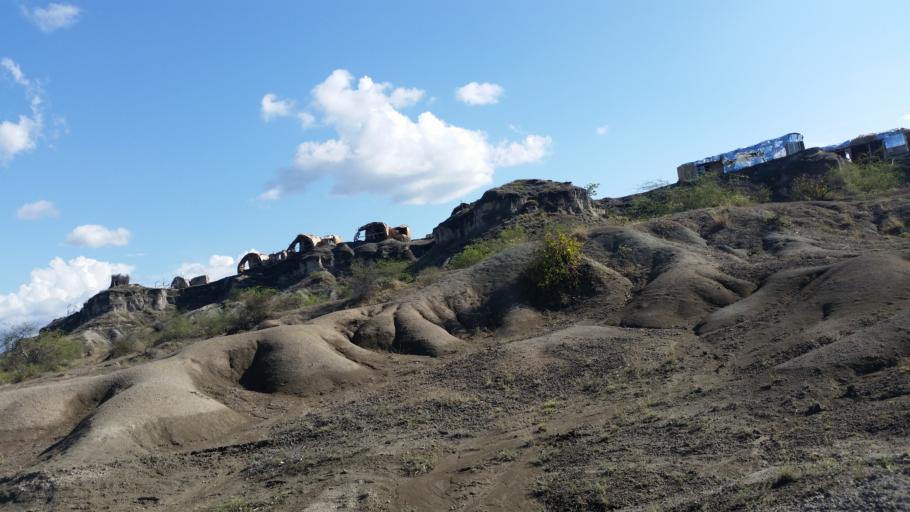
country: CO
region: Huila
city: Villavieja
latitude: 3.2539
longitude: -75.1329
